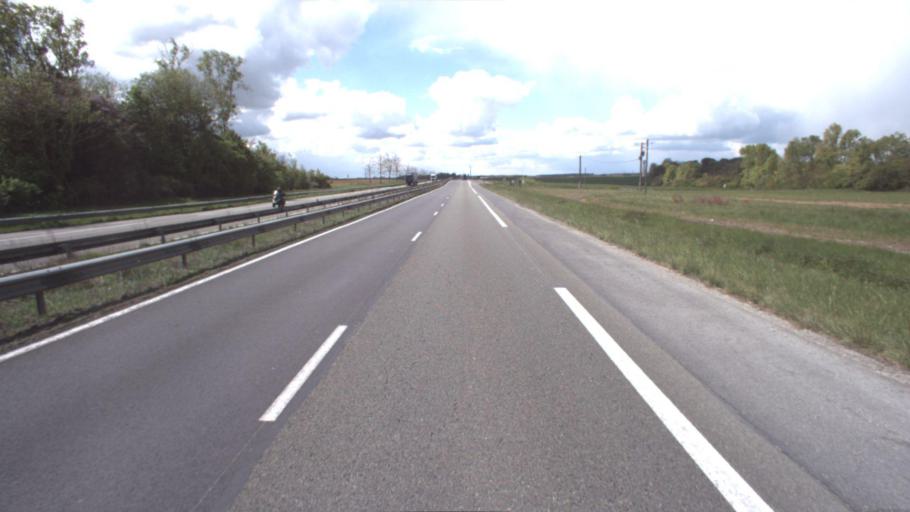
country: FR
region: Ile-de-France
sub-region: Departement de Seine-et-Marne
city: Rozay-en-Brie
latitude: 48.6861
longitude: 3.0049
